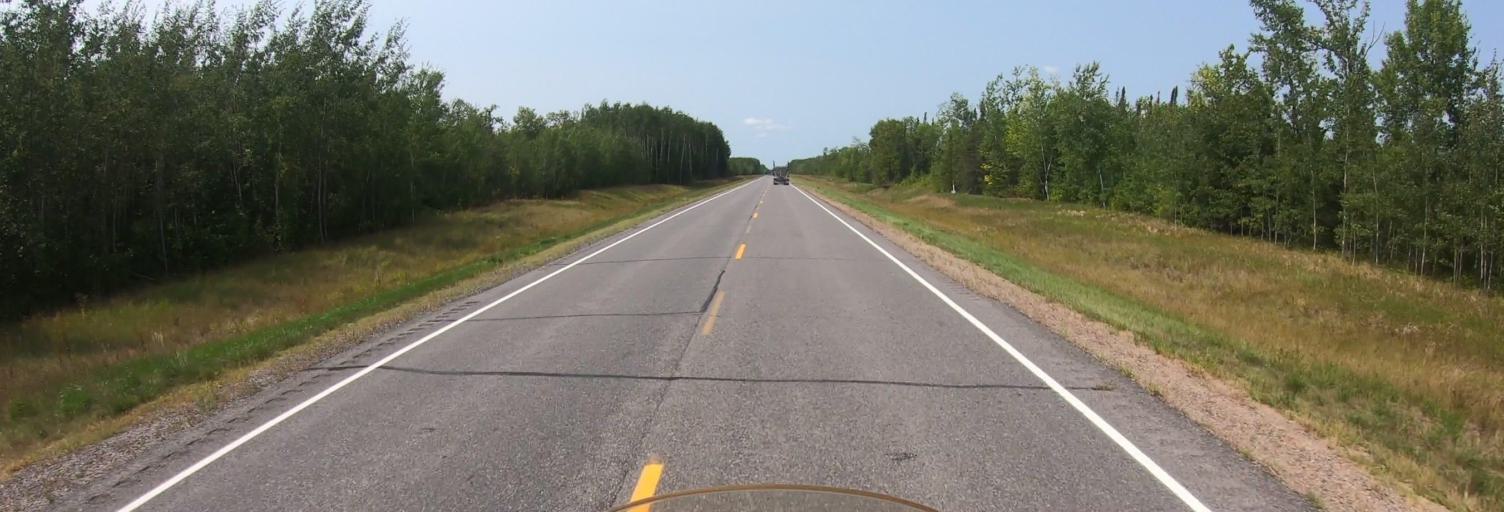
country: US
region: Minnesota
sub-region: Koochiching County
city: International Falls
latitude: 48.5127
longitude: -93.7502
